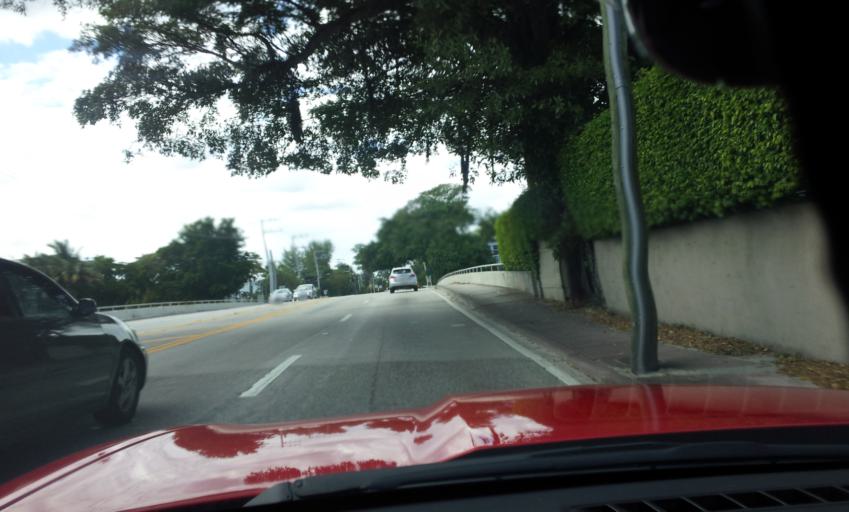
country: US
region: Florida
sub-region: Miami-Dade County
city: North Bay Village
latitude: 25.8442
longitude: -80.1239
